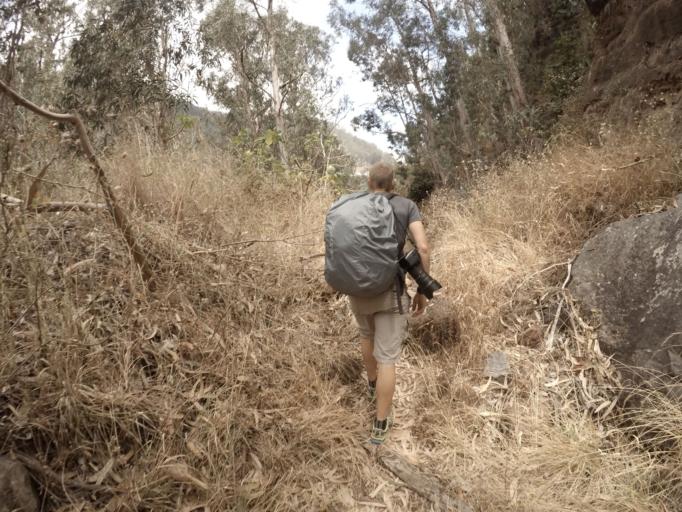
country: PT
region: Madeira
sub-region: Camara de Lobos
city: Curral das Freiras
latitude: 32.6831
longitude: -16.9616
